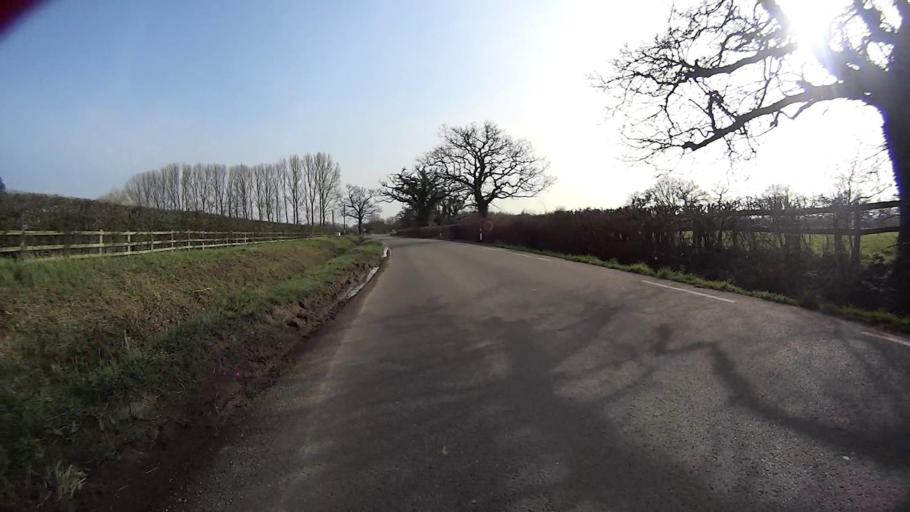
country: GB
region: England
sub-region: Surrey
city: Felbridge
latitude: 51.1834
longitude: -0.0686
